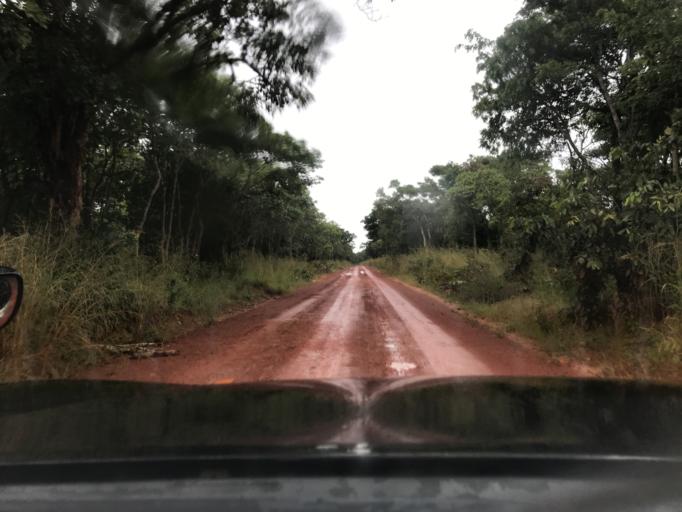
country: TZ
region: Kigoma
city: Uvinza
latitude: -5.2982
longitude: 30.3802
